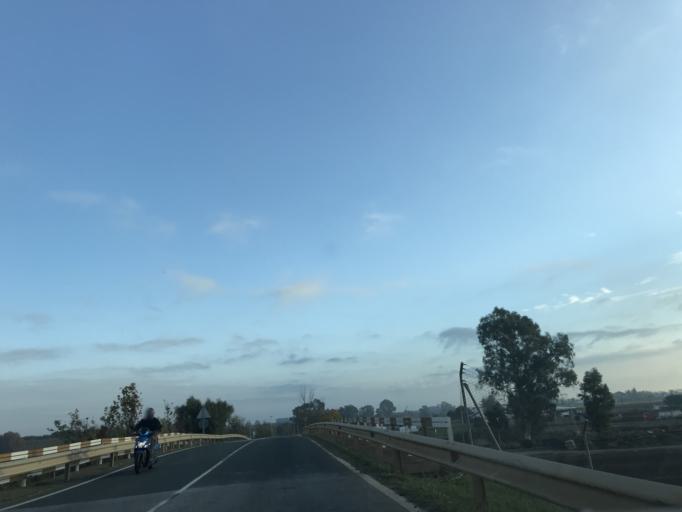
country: ES
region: Andalusia
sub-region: Provincia de Sevilla
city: Sevilla
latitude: 37.4210
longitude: -5.9493
